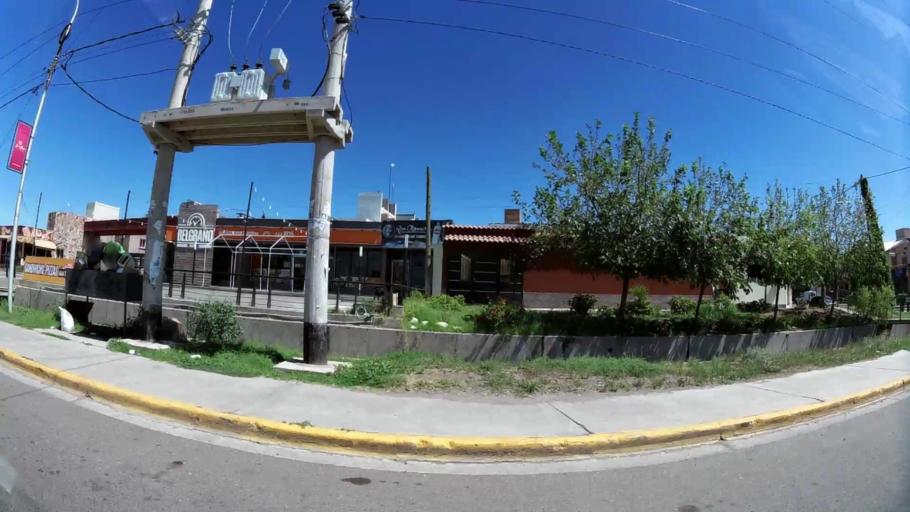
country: AR
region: Mendoza
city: Las Heras
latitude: -32.8469
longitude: -68.8609
